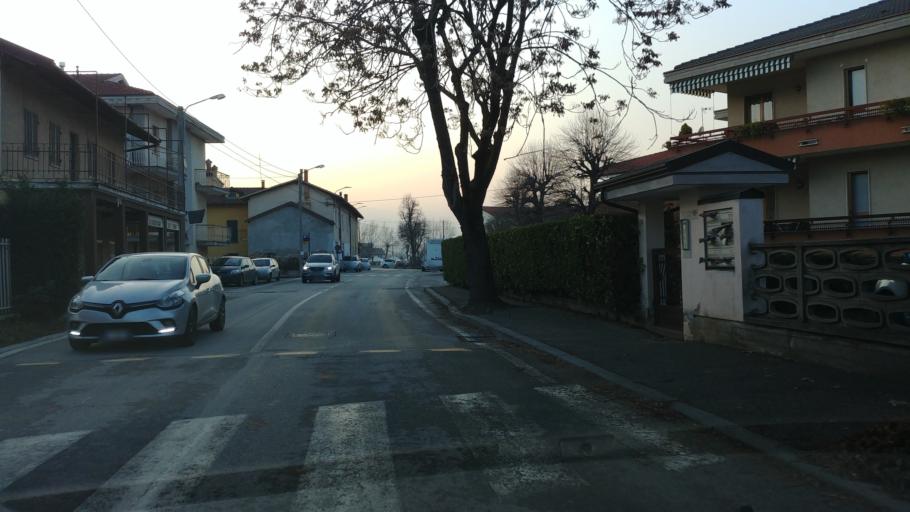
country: IT
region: Piedmont
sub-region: Provincia di Cuneo
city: Roata Rossi
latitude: 44.4322
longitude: 7.5077
